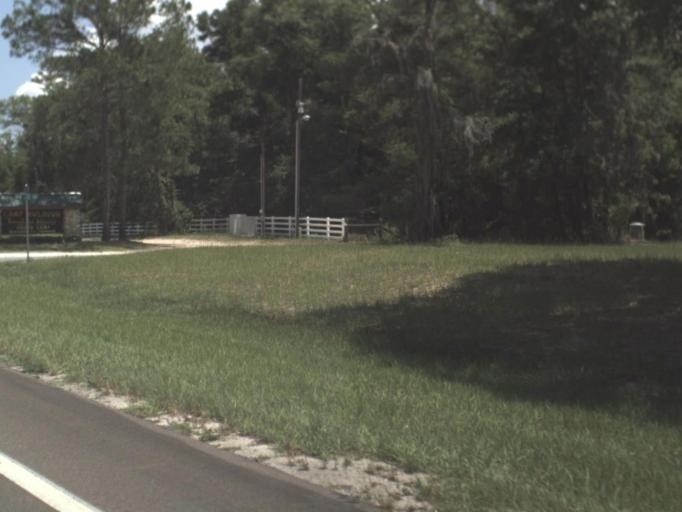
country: US
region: Florida
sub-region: Alachua County
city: High Springs
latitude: 29.8488
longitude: -82.6081
